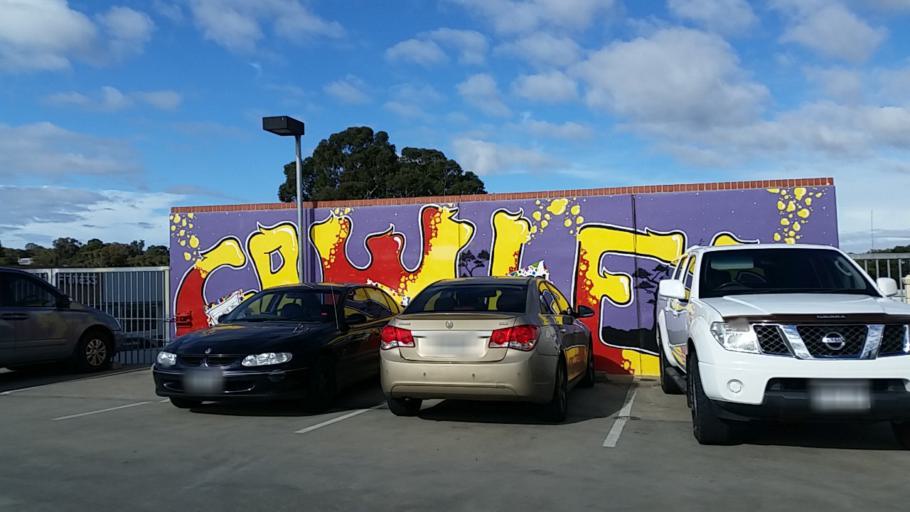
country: AU
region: South Australia
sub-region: Gawler
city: Gawler
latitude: -34.5967
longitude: 138.7479
